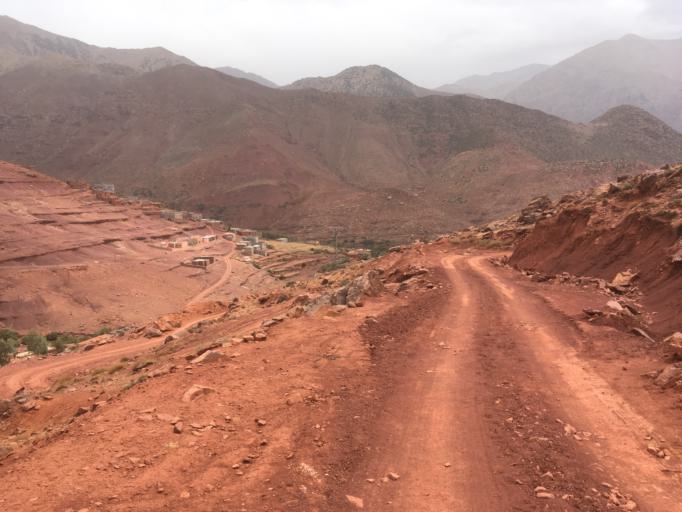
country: MA
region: Marrakech-Tensift-Al Haouz
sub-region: Al-Haouz
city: Tidili Mesfioua
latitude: 31.2769
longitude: -7.6741
